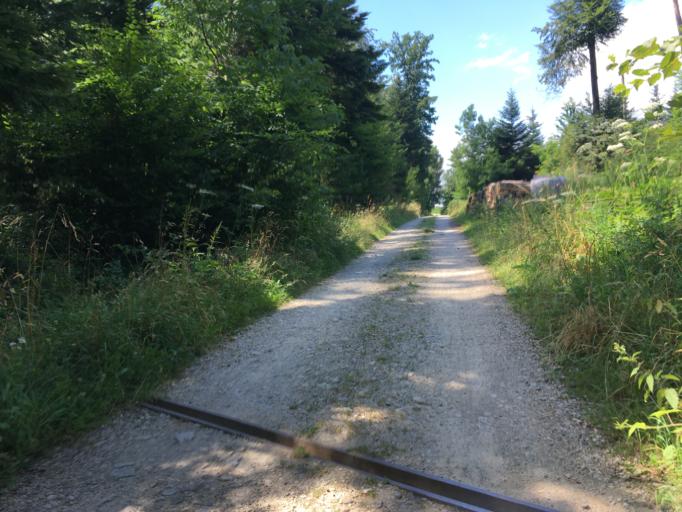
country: CH
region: Fribourg
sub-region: Broye District
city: Domdidier
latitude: 46.9332
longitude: 6.9915
